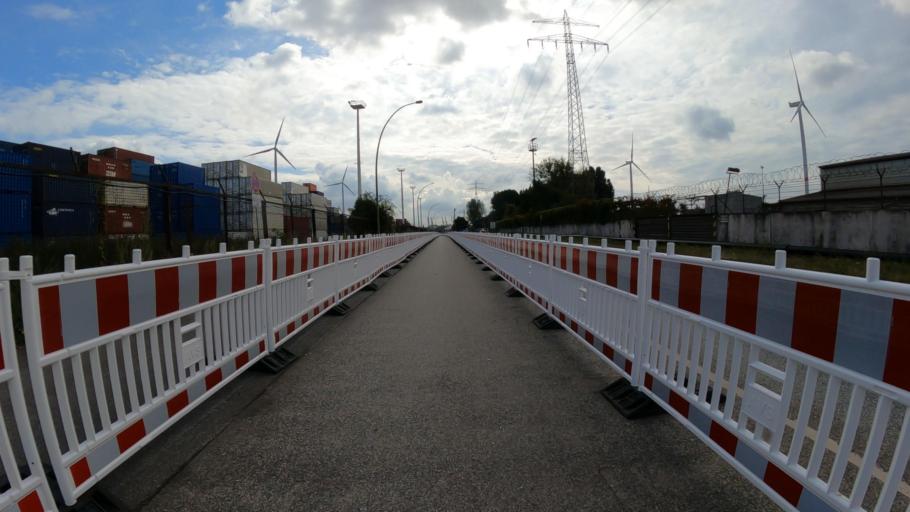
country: DE
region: Hamburg
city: Altona
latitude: 53.5233
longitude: 9.9041
